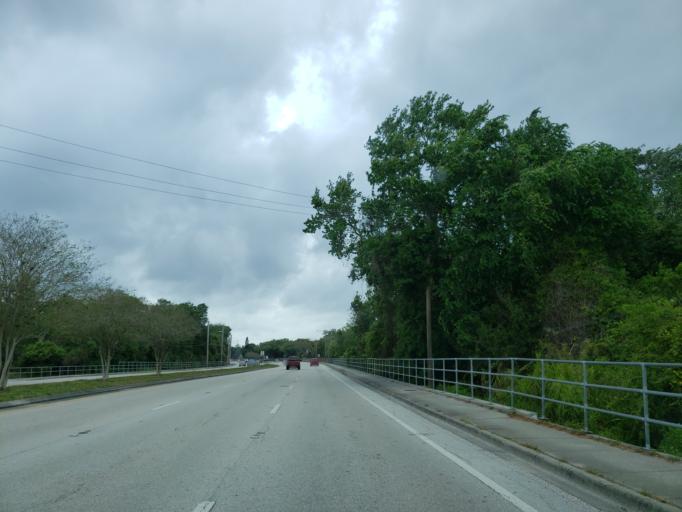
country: US
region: Florida
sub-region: Pinellas County
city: Saint George
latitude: 28.0650
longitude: -82.7156
